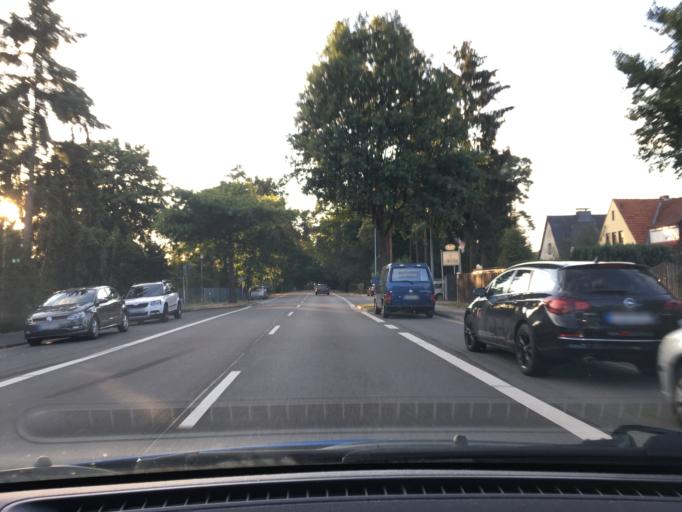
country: DE
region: Lower Saxony
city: Celle
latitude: 52.6573
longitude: 10.0563
